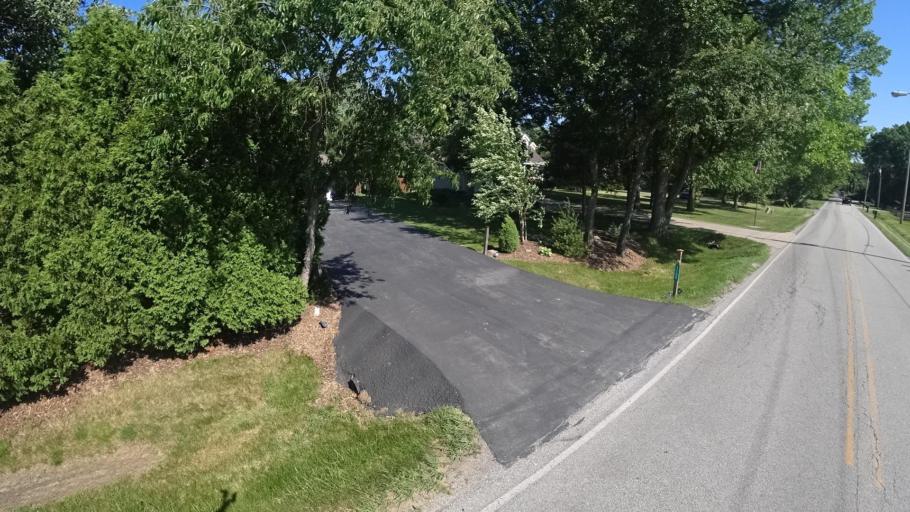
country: US
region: Indiana
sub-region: Porter County
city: Porter
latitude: 41.6022
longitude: -87.1055
